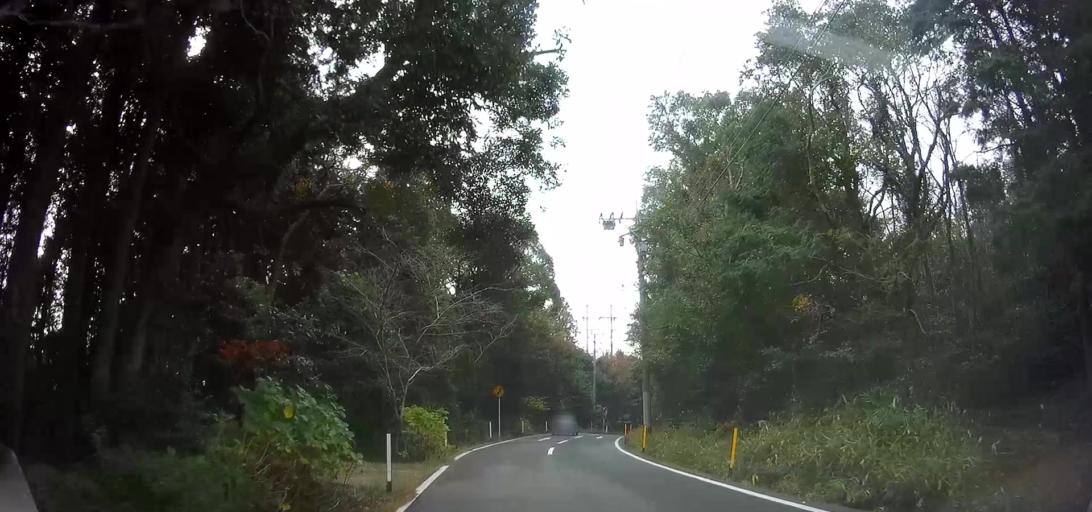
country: JP
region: Nagasaki
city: Shimabara
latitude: 32.7069
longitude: 130.2452
